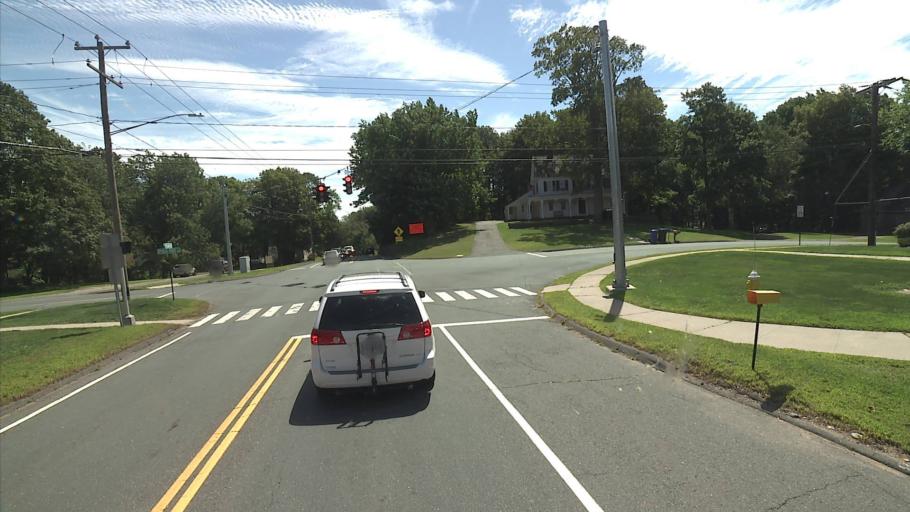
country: US
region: Connecticut
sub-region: Tolland County
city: Tolland
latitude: 41.8699
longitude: -72.3679
